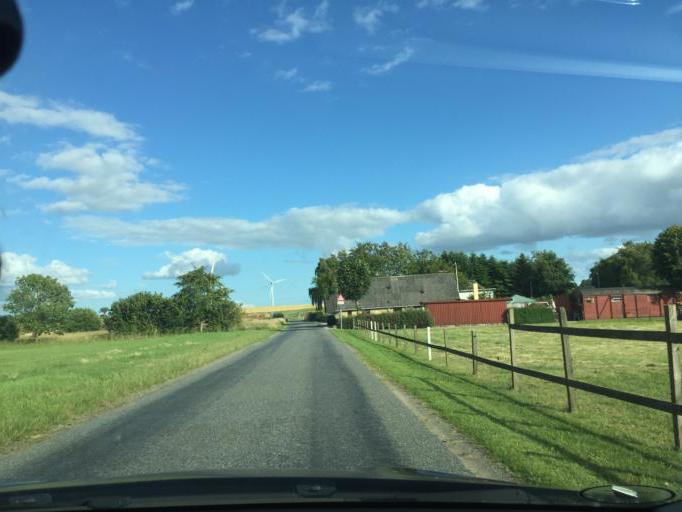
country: DK
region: South Denmark
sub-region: Faaborg-Midtfyn Kommune
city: Arslev
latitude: 55.2957
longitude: 10.5352
